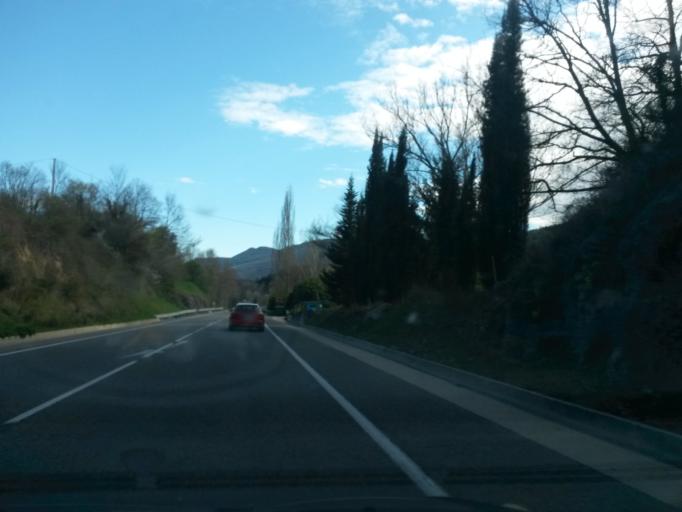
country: ES
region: Catalonia
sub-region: Provincia de Girona
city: Bas
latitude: 42.1092
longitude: 2.4906
